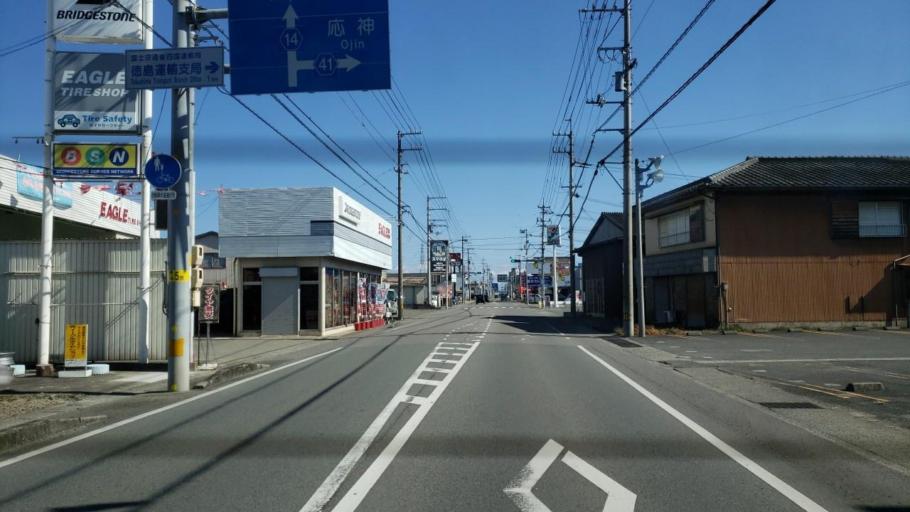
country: JP
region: Tokushima
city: Tokushima-shi
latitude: 34.1333
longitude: 134.5138
